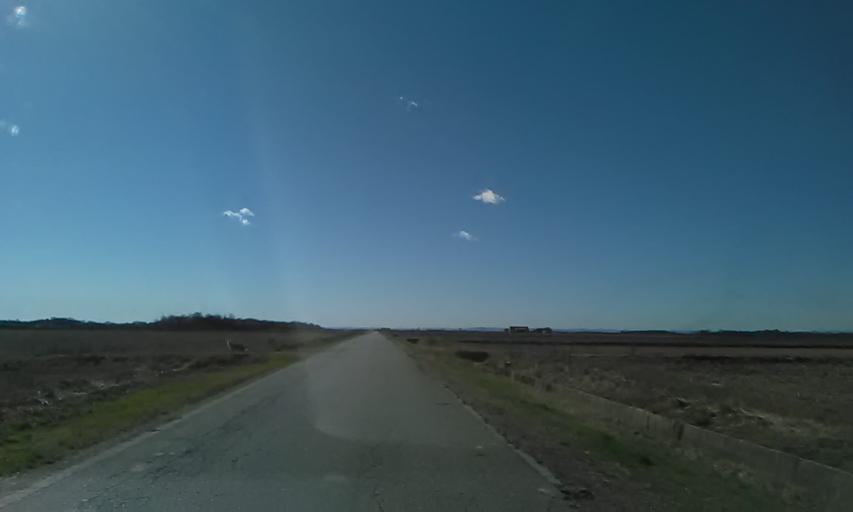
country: IT
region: Piedmont
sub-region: Provincia di Vercelli
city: Rovasenda
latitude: 45.5373
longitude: 8.2740
